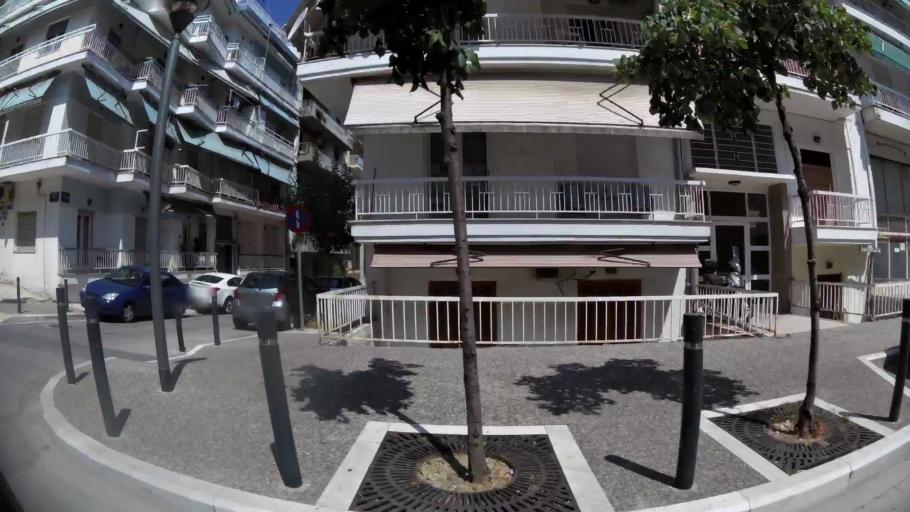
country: GR
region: Central Macedonia
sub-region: Nomos Imathias
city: Veroia
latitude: 40.5293
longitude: 22.2021
